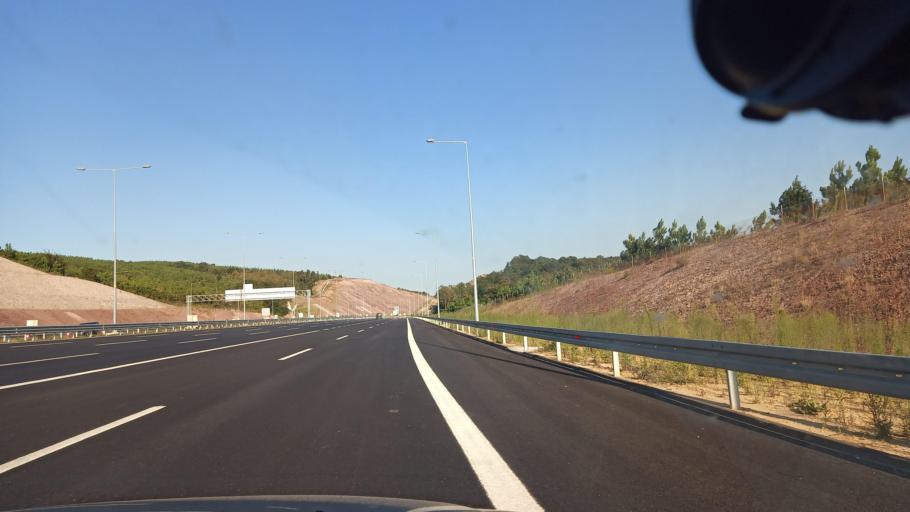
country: TR
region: Sakarya
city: Adapazari
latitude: 40.8391
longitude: 30.3687
